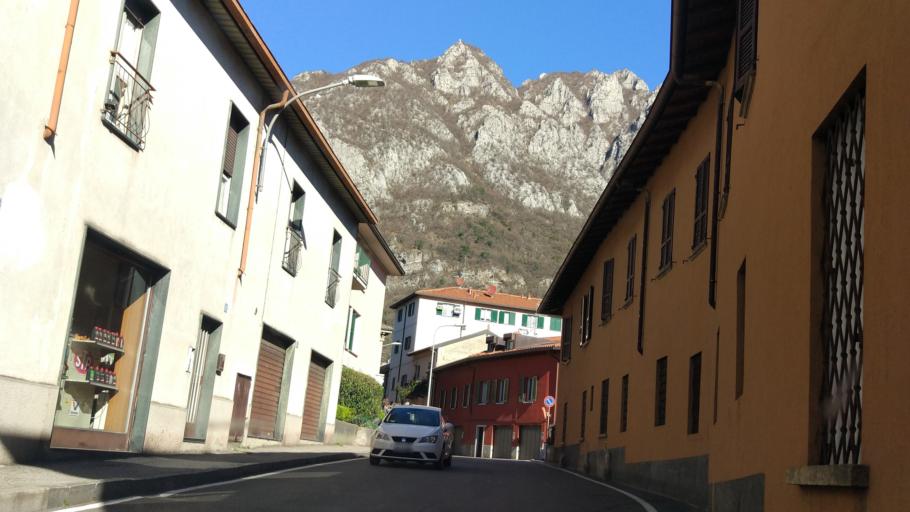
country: IT
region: Lombardy
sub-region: Provincia di Lecco
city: Lecco
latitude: 45.8618
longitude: 9.3971
